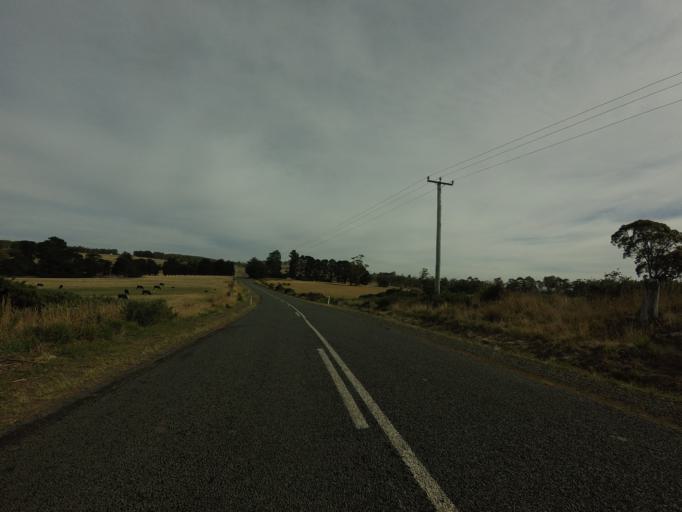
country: AU
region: Tasmania
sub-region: Brighton
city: Bridgewater
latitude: -42.3941
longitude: 147.4333
